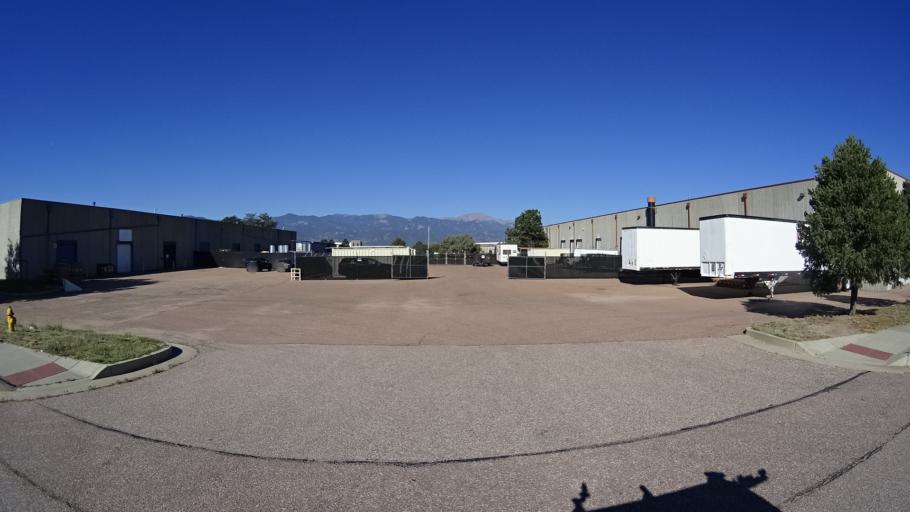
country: US
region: Colorado
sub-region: El Paso County
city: Cimarron Hills
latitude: 38.8121
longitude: -104.7236
